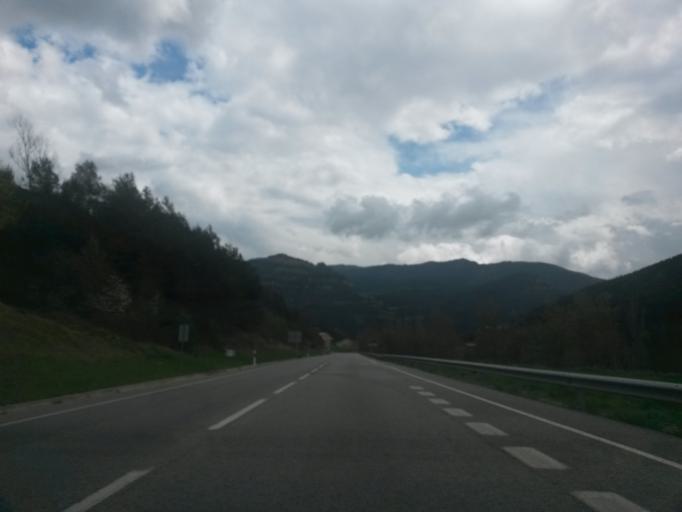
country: ES
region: Catalonia
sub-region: Provincia de Barcelona
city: Guardiola de Bergueda
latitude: 42.2445
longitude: 1.8705
